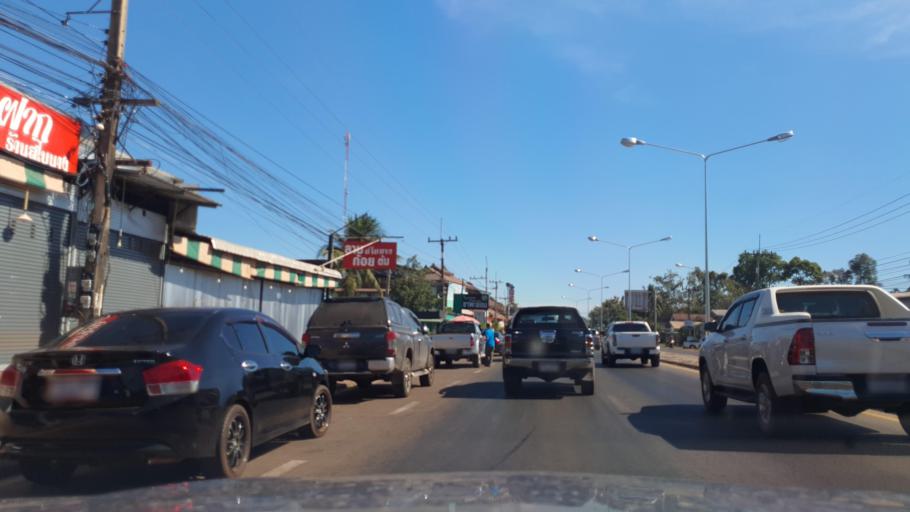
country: TH
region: Sakon Nakhon
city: Tao Ngoi
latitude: 17.0829
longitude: 104.1912
